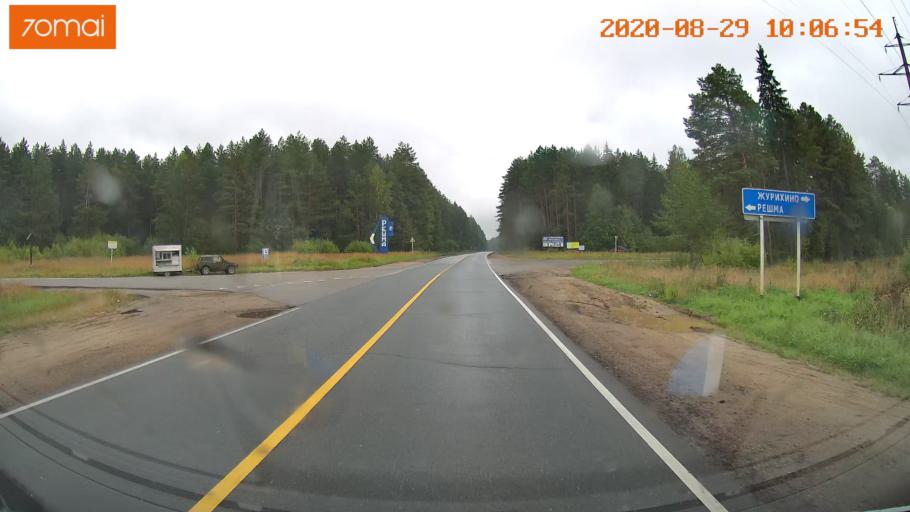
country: RU
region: Ivanovo
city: Kuznechikha
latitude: 57.3856
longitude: 42.5557
